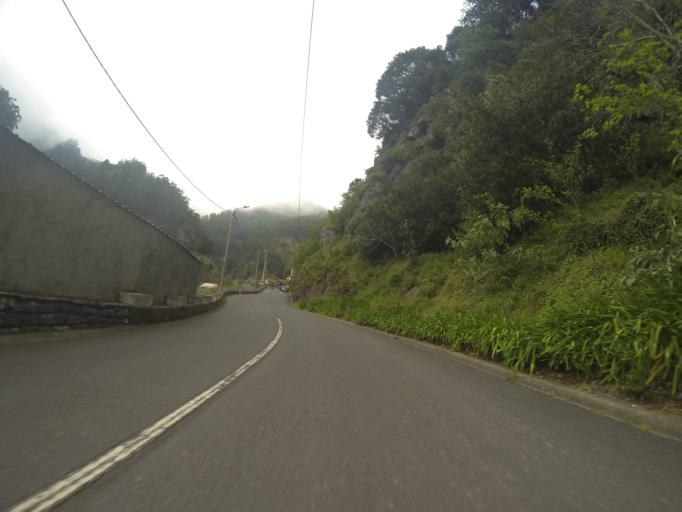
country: PT
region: Madeira
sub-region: Camara de Lobos
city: Curral das Freiras
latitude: 32.7426
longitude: -16.9656
